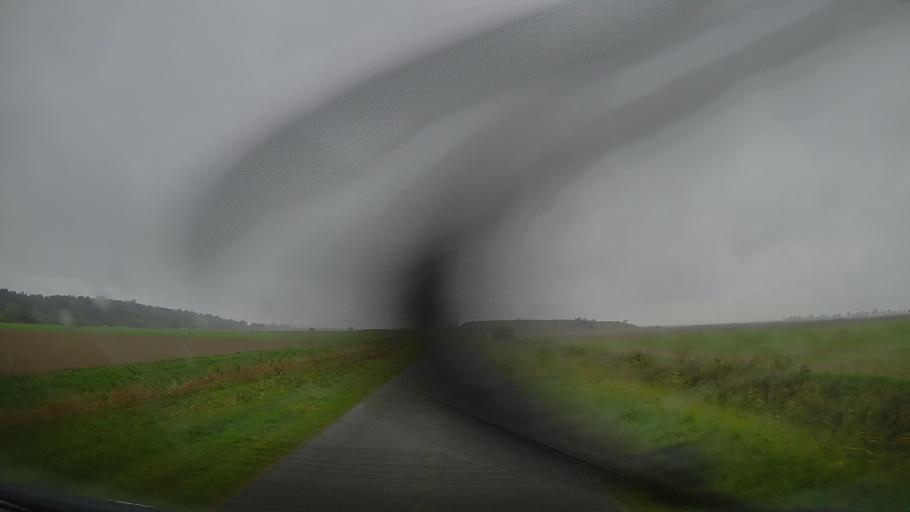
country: DE
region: Schleswig-Holstein
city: Elpersbuttel
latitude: 54.0962
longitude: 9.0010
